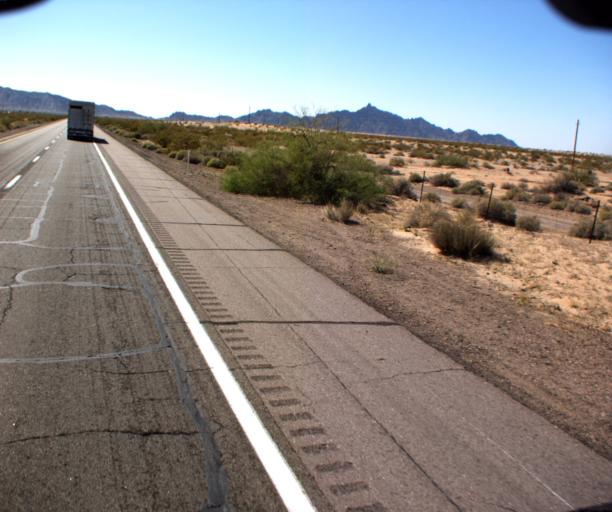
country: US
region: Arizona
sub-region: Yuma County
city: Wellton
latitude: 32.7489
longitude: -113.6672
